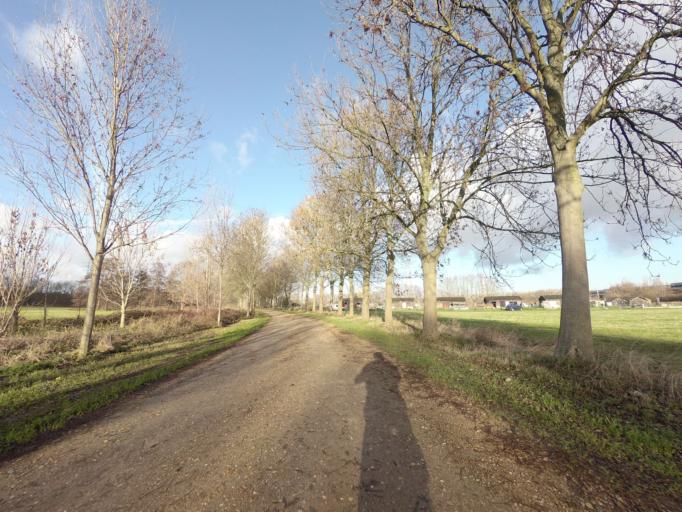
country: BE
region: Flanders
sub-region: Provincie Antwerpen
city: Kapellen
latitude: 51.2853
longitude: 4.4077
